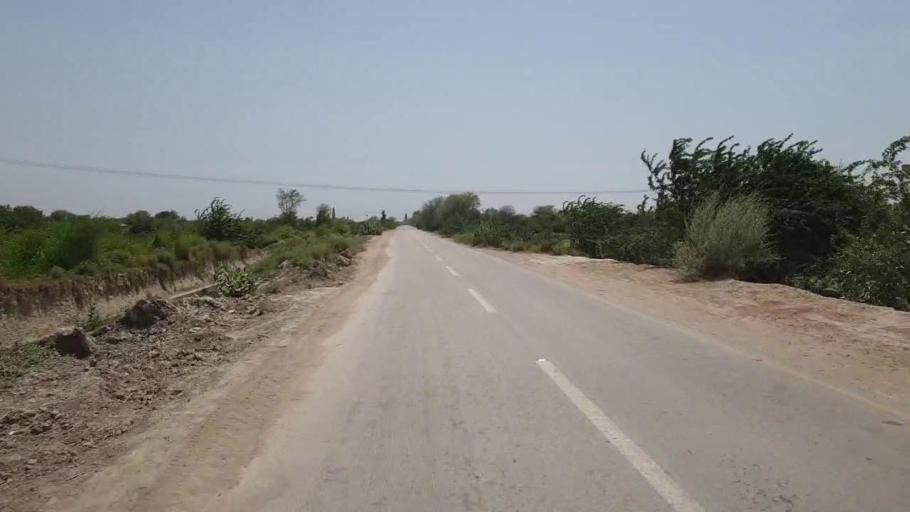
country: PK
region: Sindh
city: Daur
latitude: 26.3458
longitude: 68.1314
